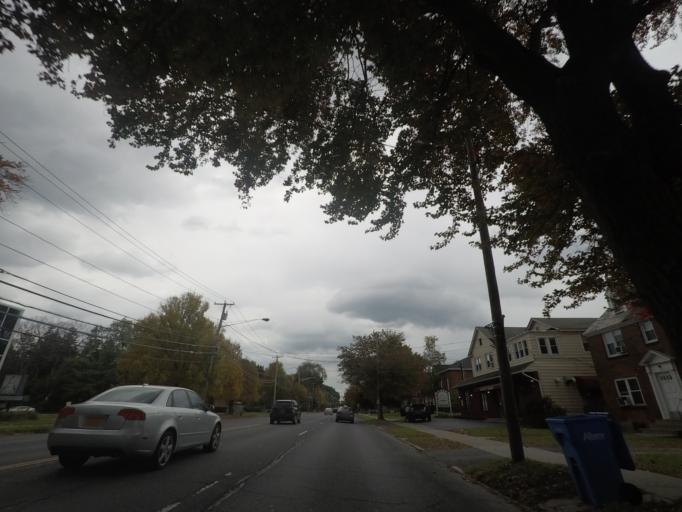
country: US
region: New York
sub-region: Albany County
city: Roessleville
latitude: 42.6759
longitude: -73.8217
